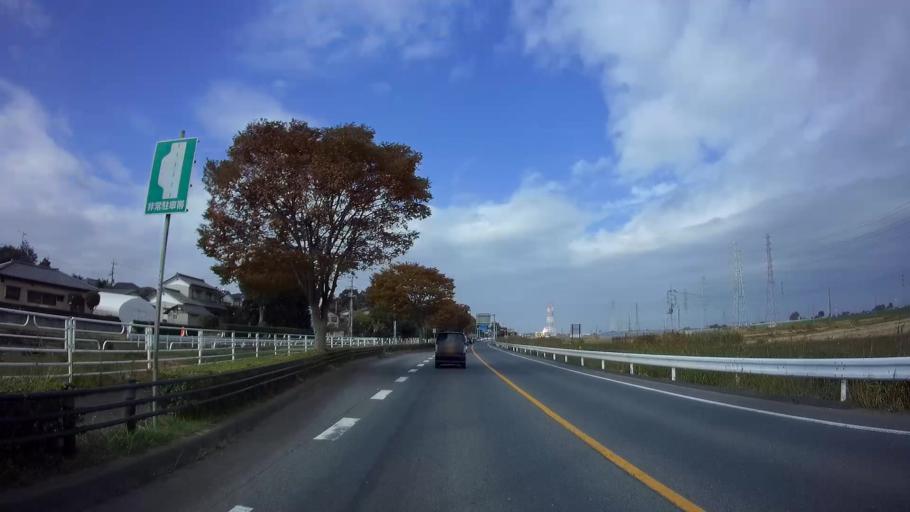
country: JP
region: Gunma
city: Sakai-nakajima
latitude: 36.2199
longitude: 139.2385
